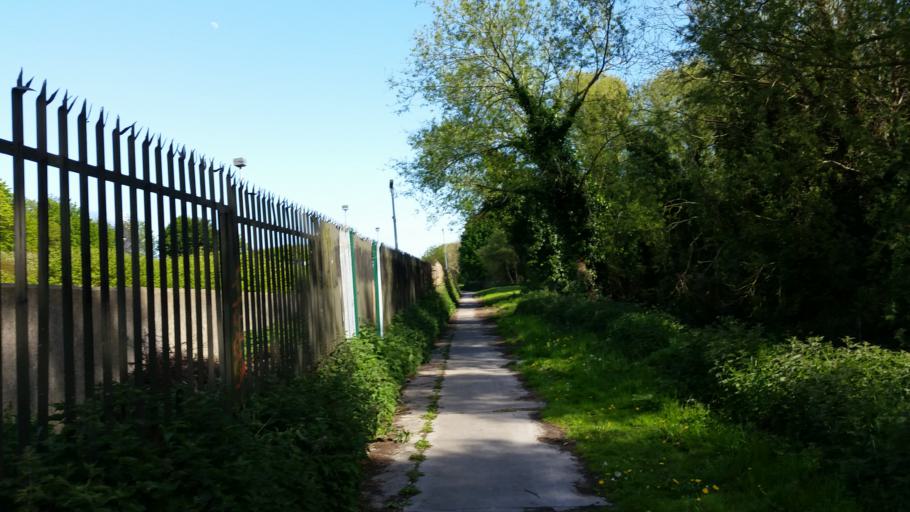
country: IE
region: Leinster
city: Beaumont
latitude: 53.4027
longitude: -6.2319
